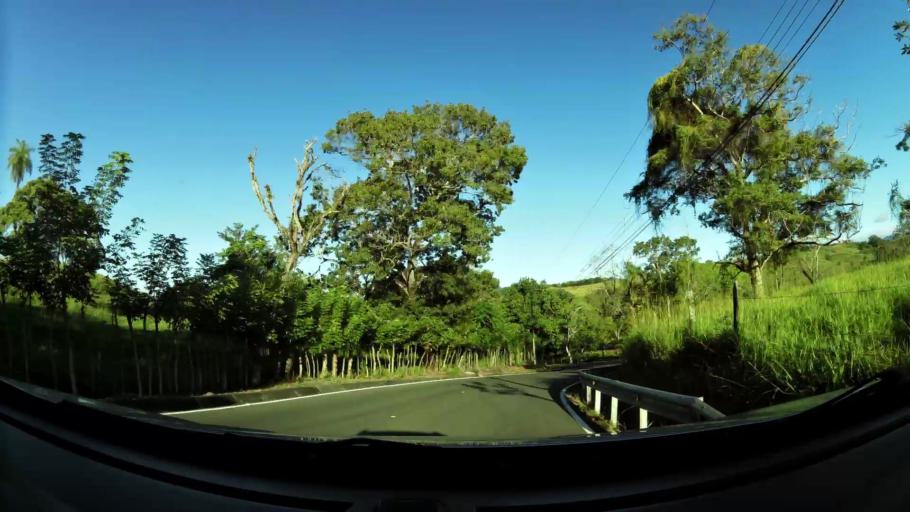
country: CR
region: Puntarenas
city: Miramar
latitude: 10.1421
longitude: -84.8460
